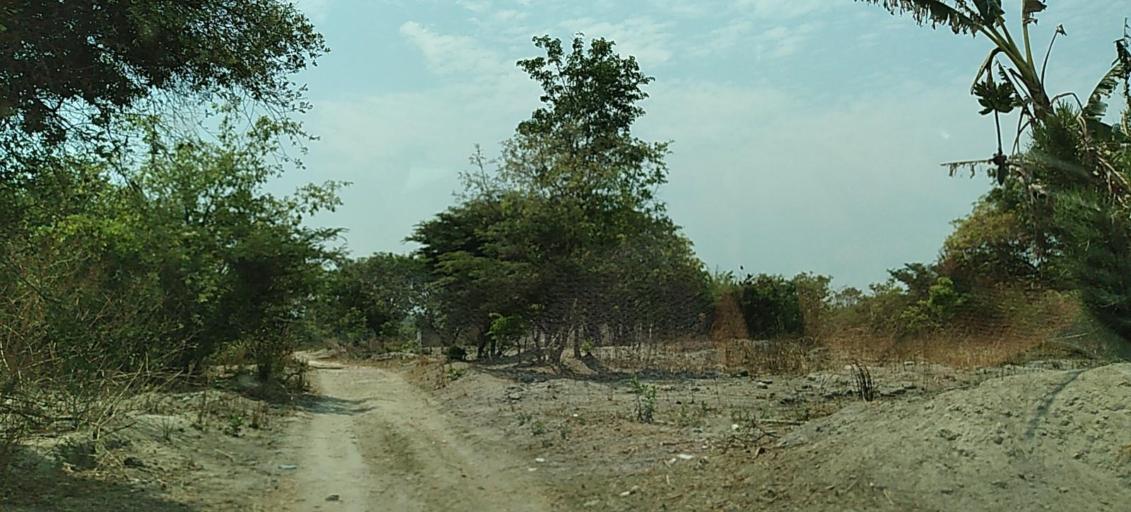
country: ZM
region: Copperbelt
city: Kalulushi
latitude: -12.9451
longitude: 28.1258
